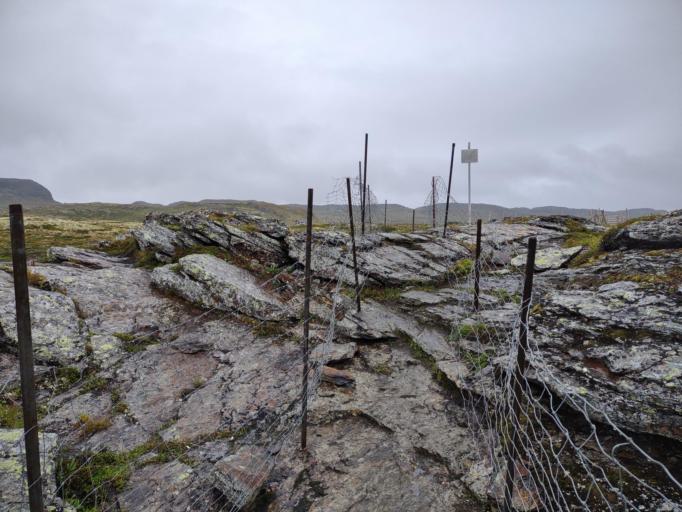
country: NO
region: Hordaland
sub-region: Eidfjord
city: Eidfjord
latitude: 60.0931
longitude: 7.1267
